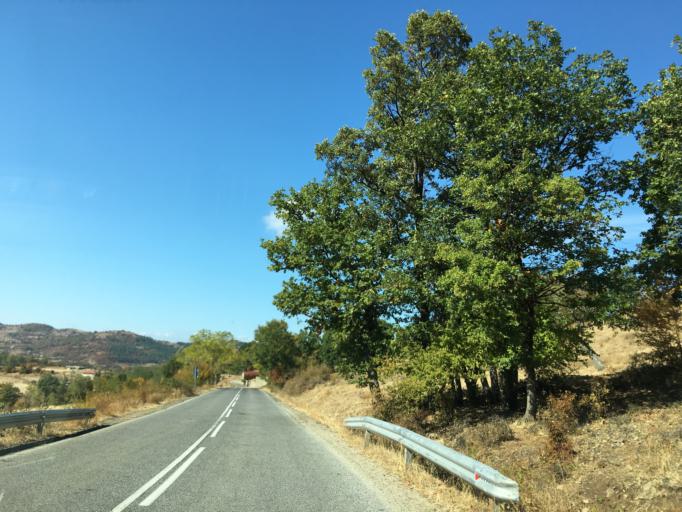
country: BG
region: Kurdzhali
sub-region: Obshtina Krumovgrad
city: Krumovgrad
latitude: 41.4716
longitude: 25.5293
